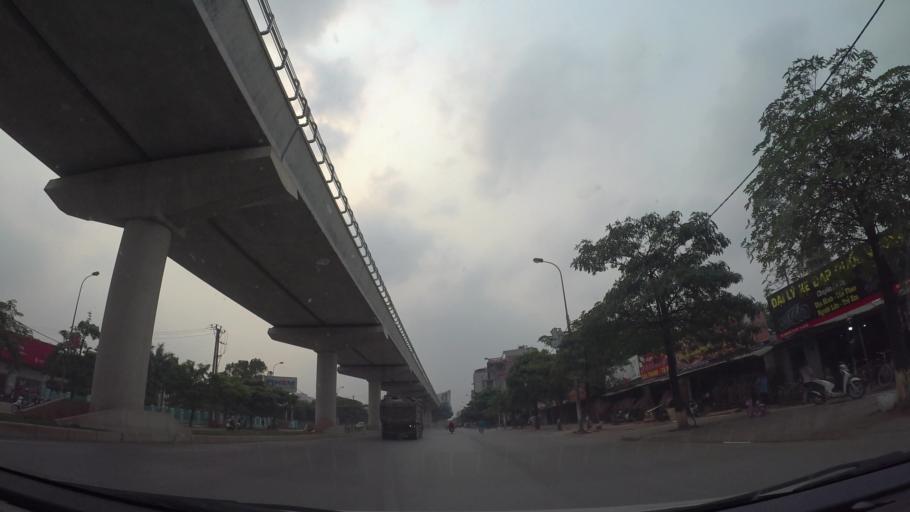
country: VN
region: Ha Noi
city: Cau Dien
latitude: 21.0469
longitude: 105.7476
